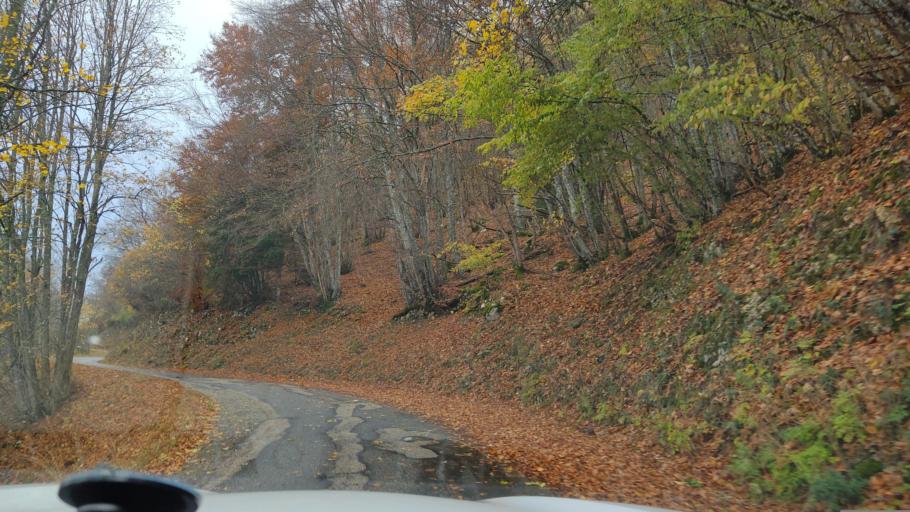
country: FR
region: Rhone-Alpes
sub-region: Departement de la Savoie
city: Le Bourget-du-Lac
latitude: 45.6465
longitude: 5.8098
